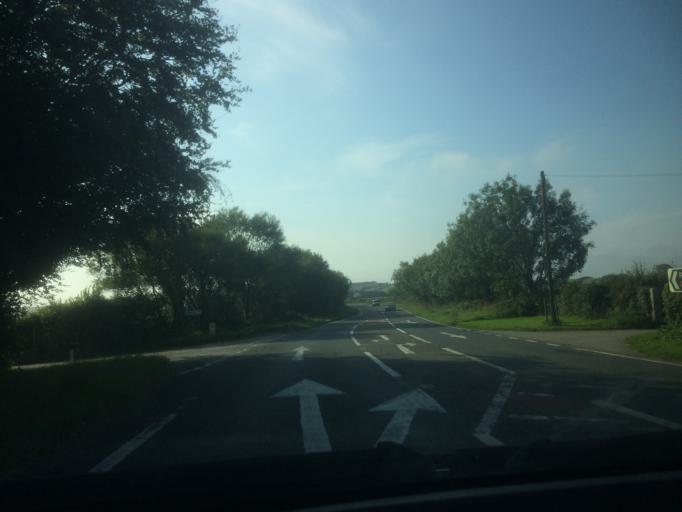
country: GB
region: England
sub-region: Cornwall
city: Callington
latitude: 50.4928
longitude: -4.2902
